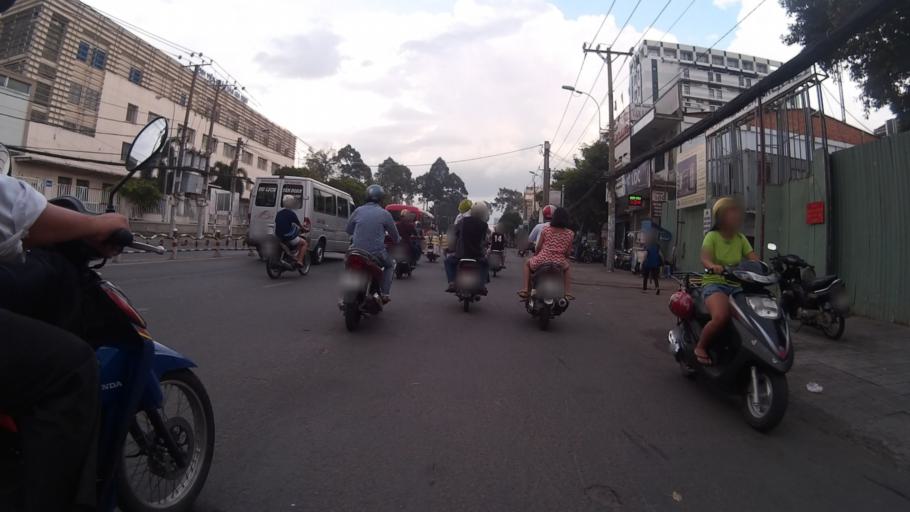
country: VN
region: Ho Chi Minh City
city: Quan Binh Thanh
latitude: 10.8031
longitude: 106.6934
